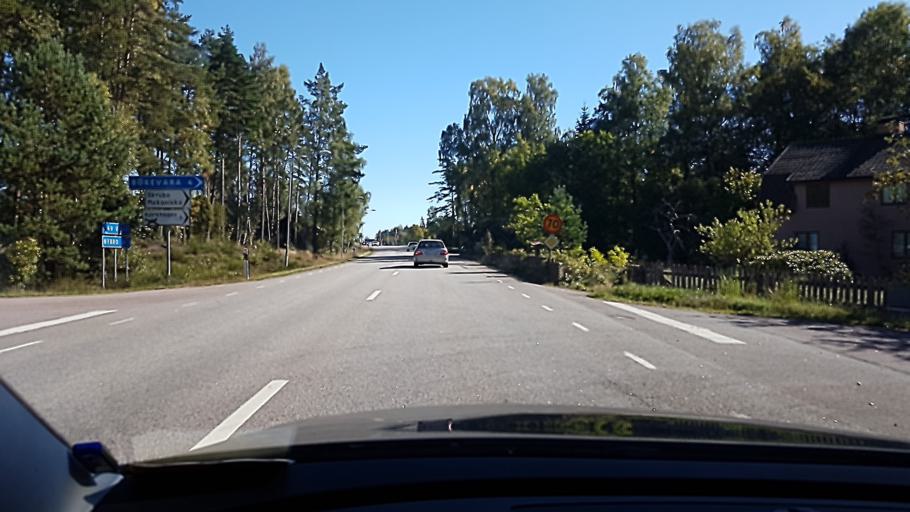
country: SE
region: Kalmar
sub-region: Emmaboda Kommun
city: Emmaboda
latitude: 56.7336
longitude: 15.4777
